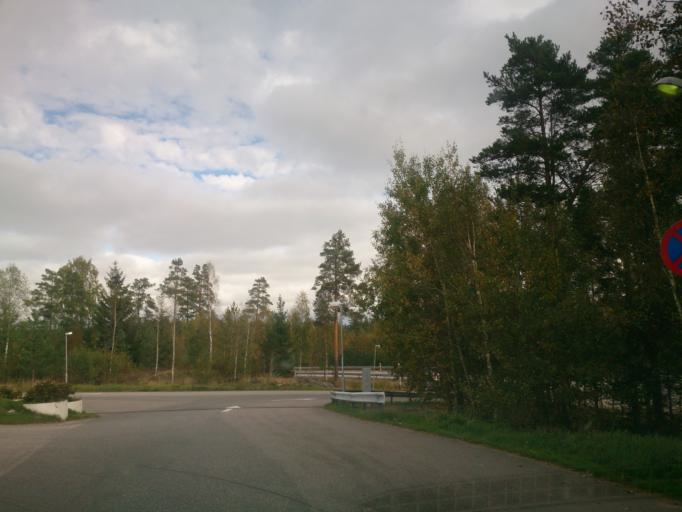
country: SE
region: OEstergoetland
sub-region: Norrkopings Kommun
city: Krokek
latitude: 58.7300
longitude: 16.4110
